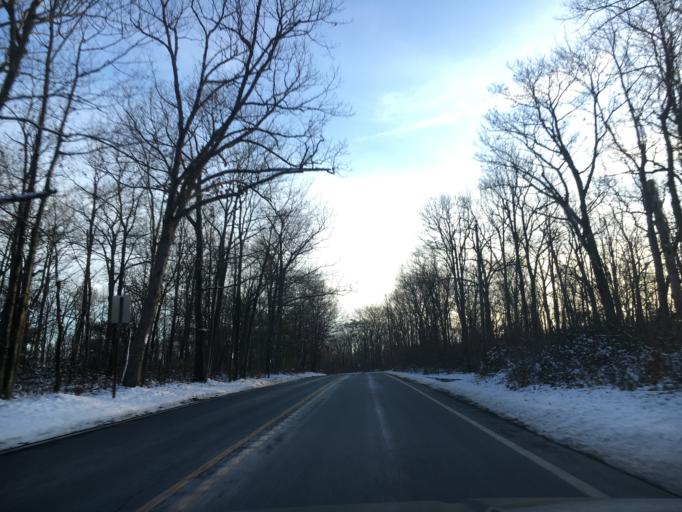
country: US
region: Pennsylvania
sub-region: Pike County
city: Hemlock Farms
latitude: 41.3586
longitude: -75.1286
